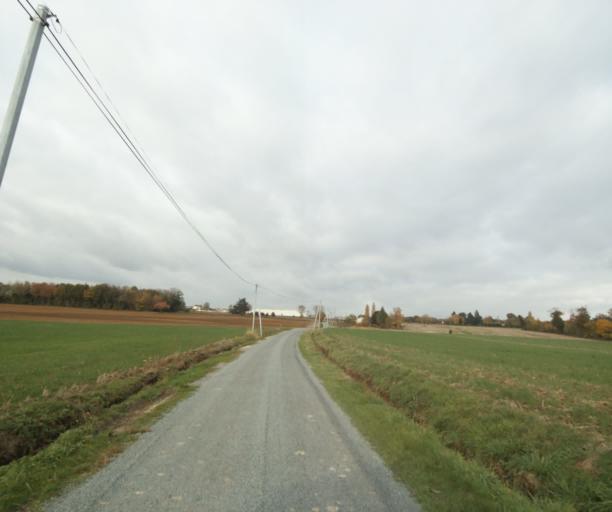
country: FR
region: Poitou-Charentes
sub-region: Departement de la Charente-Maritime
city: Saint-Georges-des-Coteaux
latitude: 45.7884
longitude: -0.7302
